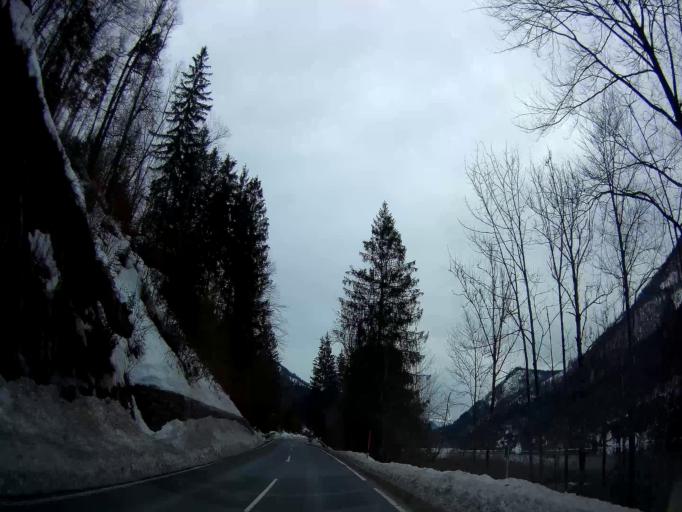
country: AT
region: Salzburg
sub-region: Politischer Bezirk Salzburg-Umgebung
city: Ebenau
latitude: 47.7594
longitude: 13.1808
